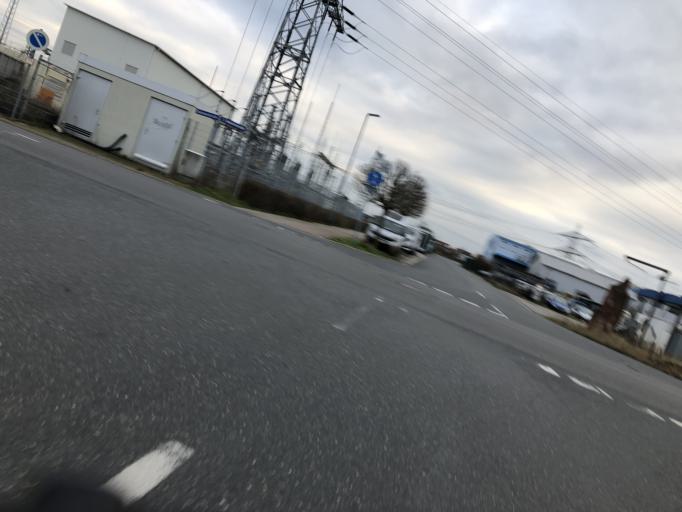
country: DE
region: Baden-Wuerttemberg
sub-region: Karlsruhe Region
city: Neulussheim
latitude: 49.2936
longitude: 8.5098
